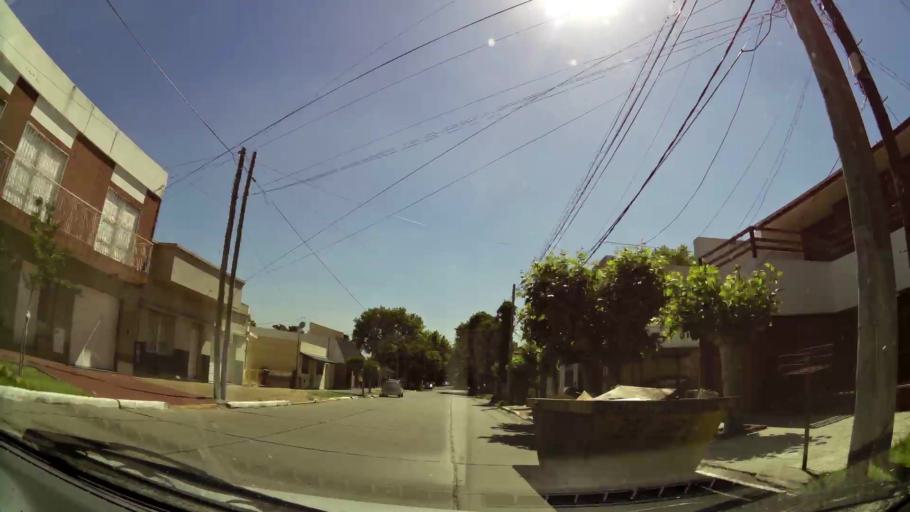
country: AR
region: Buenos Aires
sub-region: Partido de Quilmes
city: Quilmes
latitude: -34.7089
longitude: -58.2904
